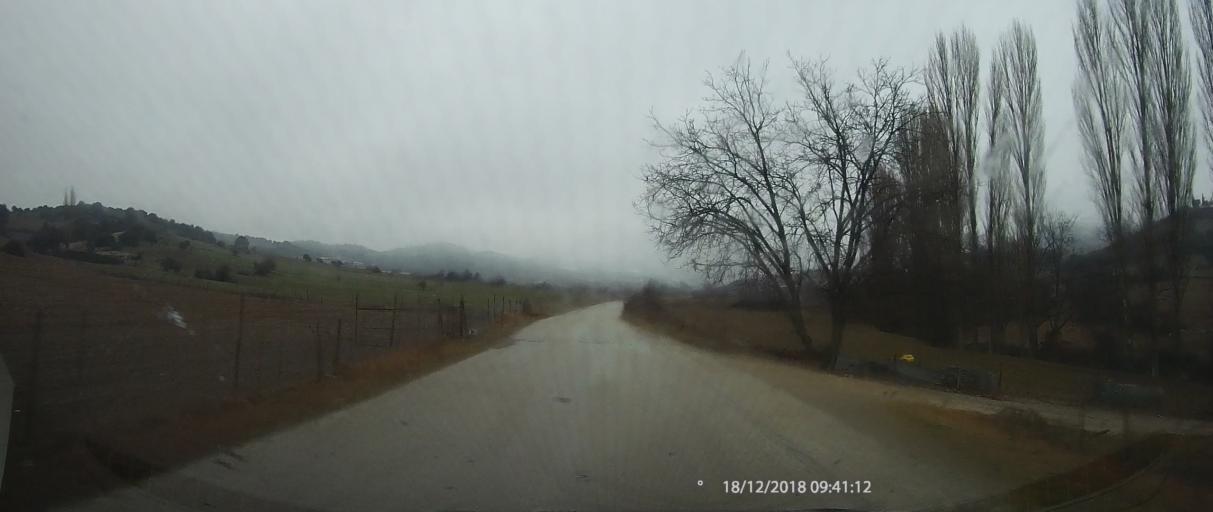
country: GR
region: Thessaly
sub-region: Nomos Larisis
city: Elassona
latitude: 40.0094
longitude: 22.2312
